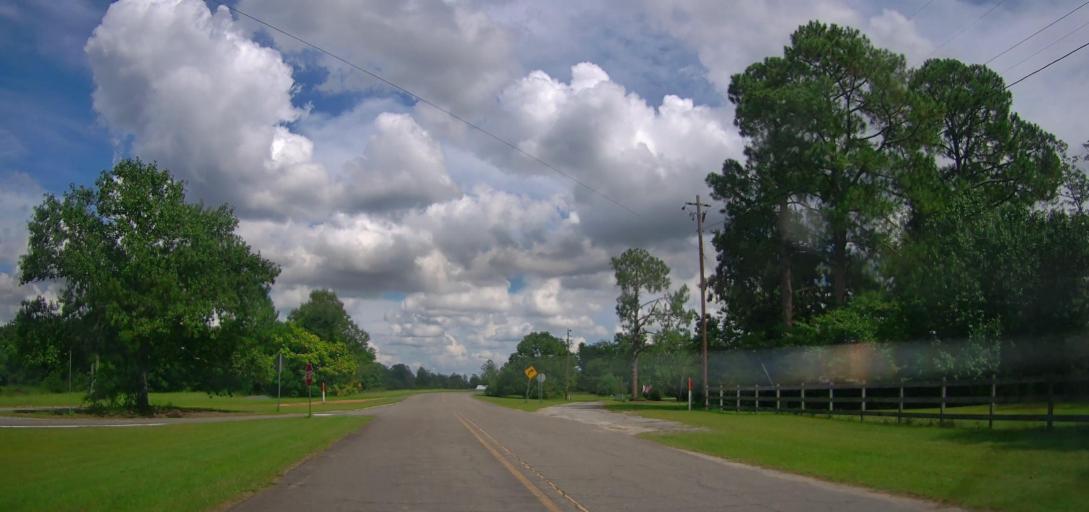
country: US
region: Georgia
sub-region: Taylor County
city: Butler
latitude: 32.5961
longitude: -84.3838
